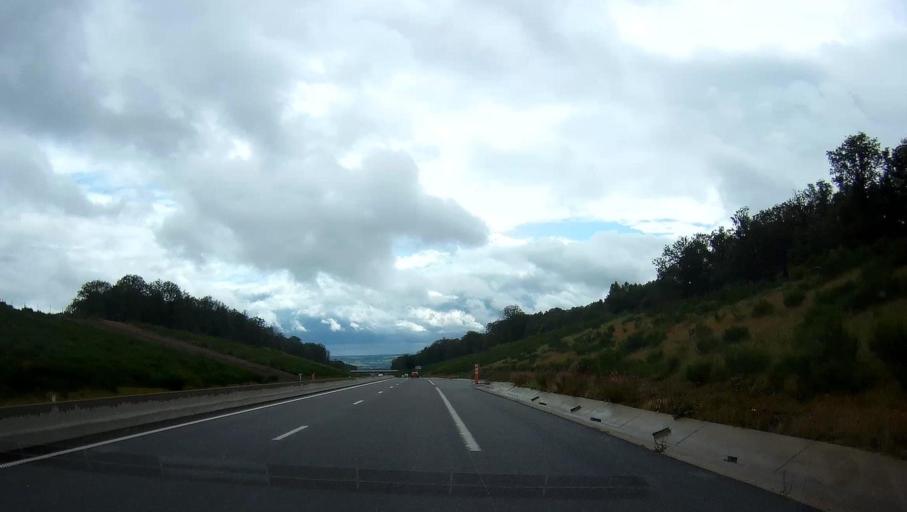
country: FR
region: Champagne-Ardenne
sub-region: Departement des Ardennes
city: Rimogne
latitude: 49.8633
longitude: 4.5102
